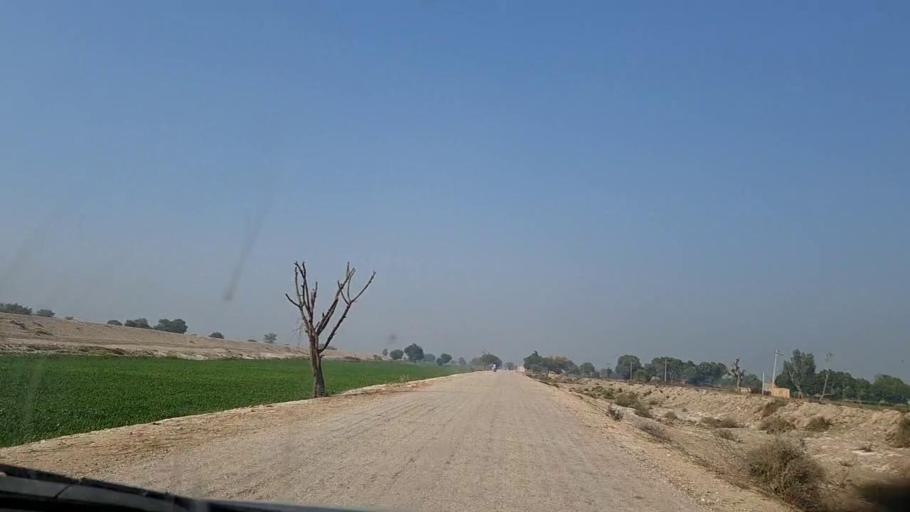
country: PK
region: Sindh
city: Moro
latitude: 26.7282
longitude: 67.9212
